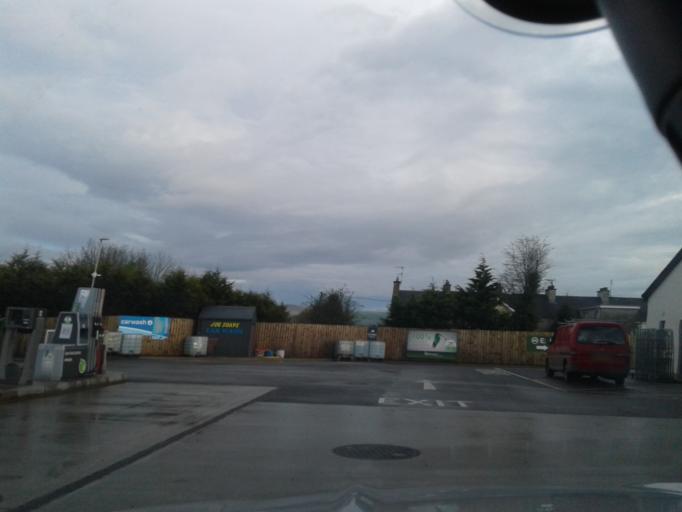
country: IE
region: Ulster
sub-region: County Donegal
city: Leifear
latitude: 54.8366
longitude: -7.4883
